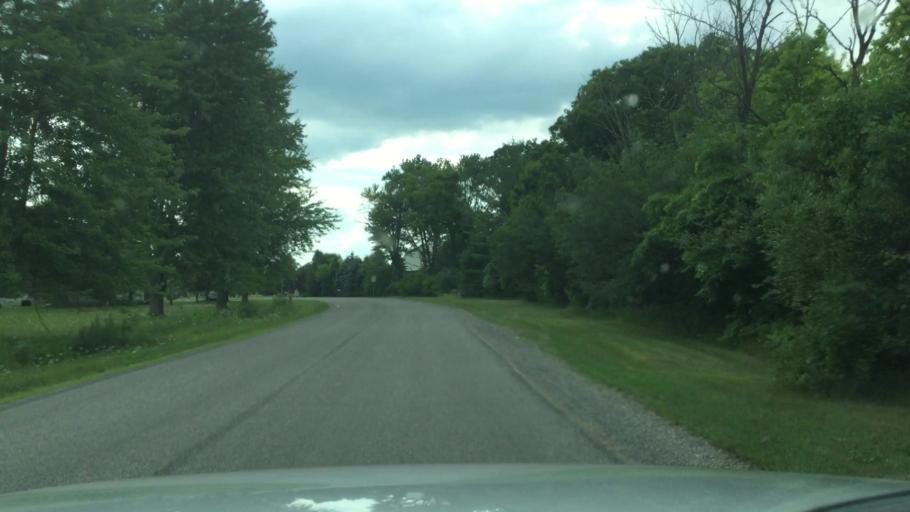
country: US
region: Michigan
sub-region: Saginaw County
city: Frankenmuth
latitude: 43.3215
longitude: -83.8069
